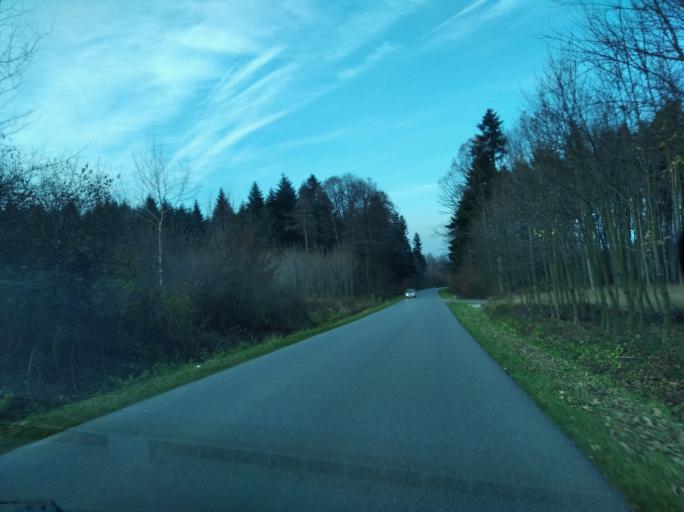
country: PL
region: Subcarpathian Voivodeship
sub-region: Powiat ropczycko-sedziszowski
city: Zagorzyce
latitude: 49.9653
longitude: 21.6959
